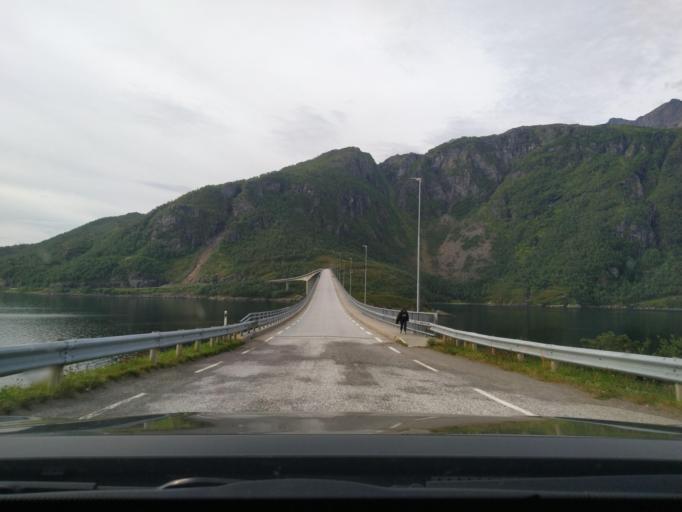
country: NO
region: Troms
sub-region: Dyroy
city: Brostadbotn
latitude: 68.8936
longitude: 17.4646
